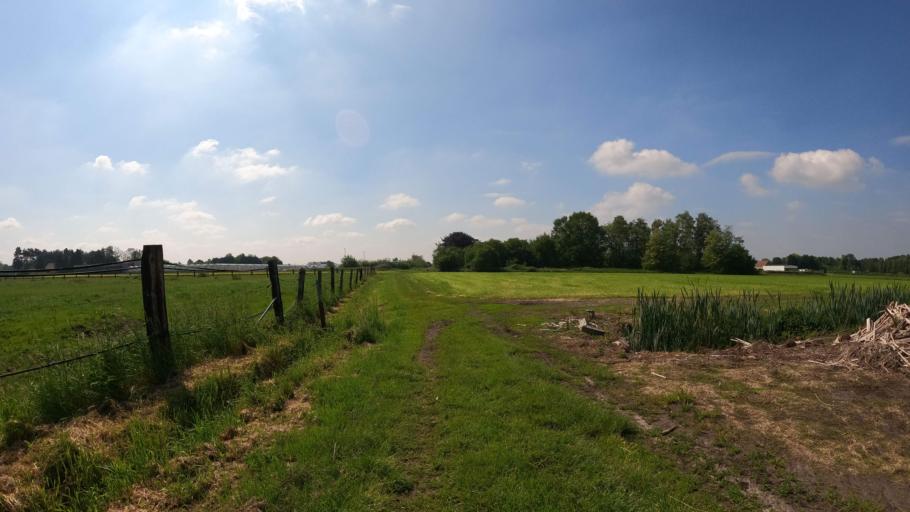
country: BE
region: Flanders
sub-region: Provincie Antwerpen
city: Duffel
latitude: 51.0844
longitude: 4.5188
